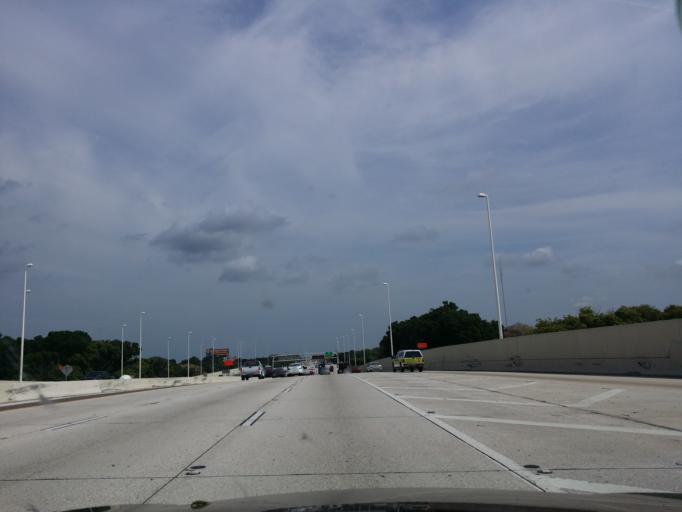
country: US
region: Florida
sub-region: Hillsborough County
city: Tampa
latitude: 27.9675
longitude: -82.4533
